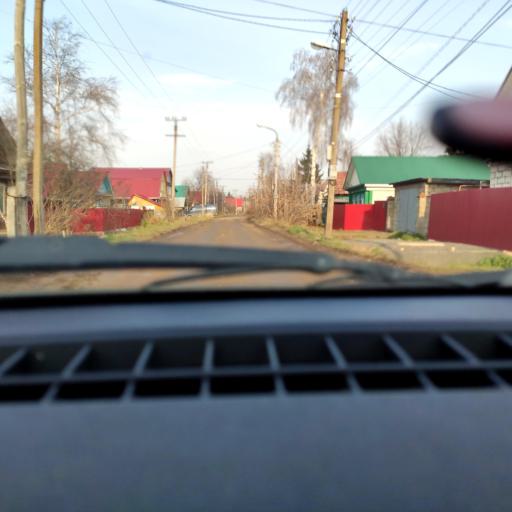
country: RU
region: Bashkortostan
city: Iglino
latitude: 54.8229
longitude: 56.1858
